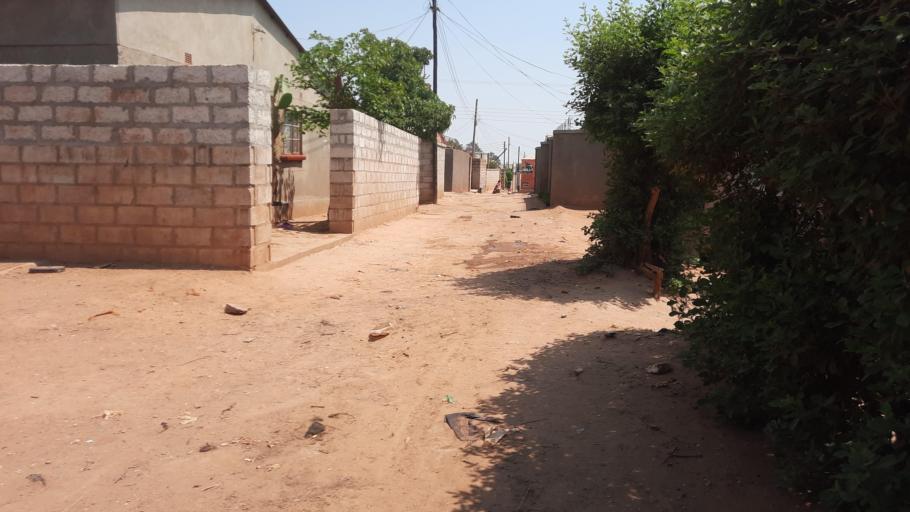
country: ZM
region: Lusaka
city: Lusaka
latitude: -15.3964
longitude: 28.3746
